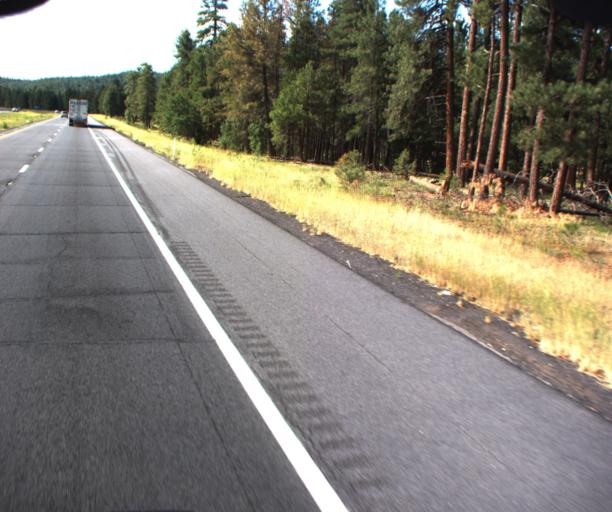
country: US
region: Arizona
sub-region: Coconino County
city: Sedona
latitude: 34.9627
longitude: -111.6807
